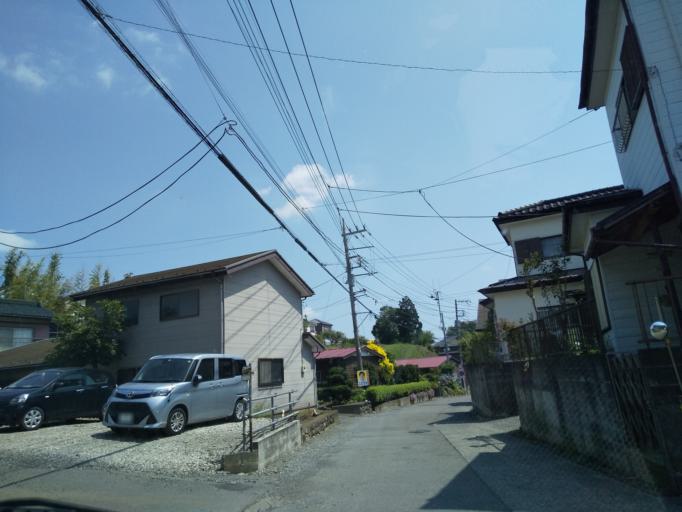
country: JP
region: Kanagawa
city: Zama
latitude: 35.5060
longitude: 139.3903
